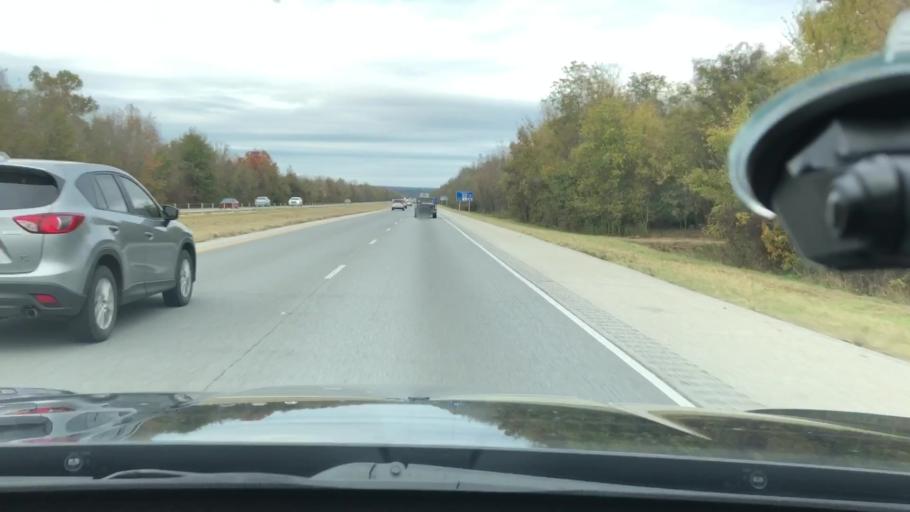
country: US
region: Arkansas
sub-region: Clark County
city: Arkadelphia
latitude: 34.1567
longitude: -93.0774
